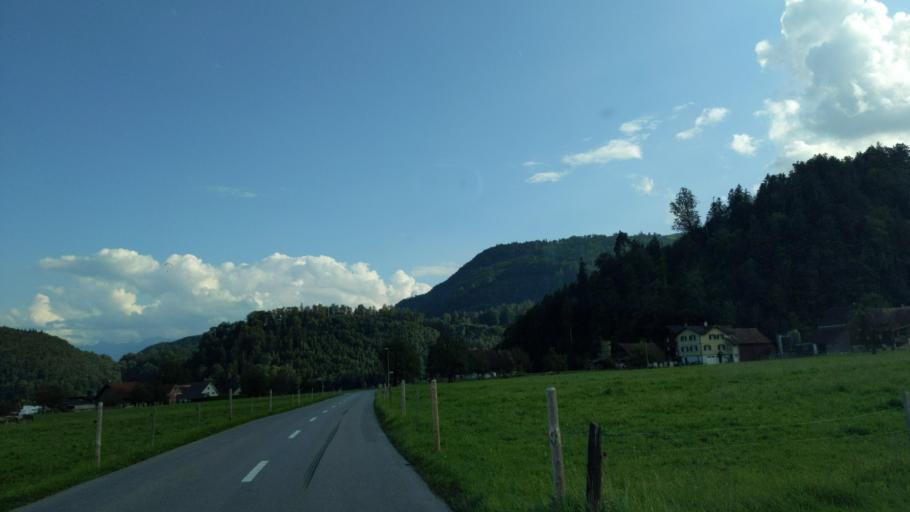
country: CH
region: Saint Gallen
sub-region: Wahlkreis Rheintal
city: Eichberg
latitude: 47.3371
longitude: 9.5333
